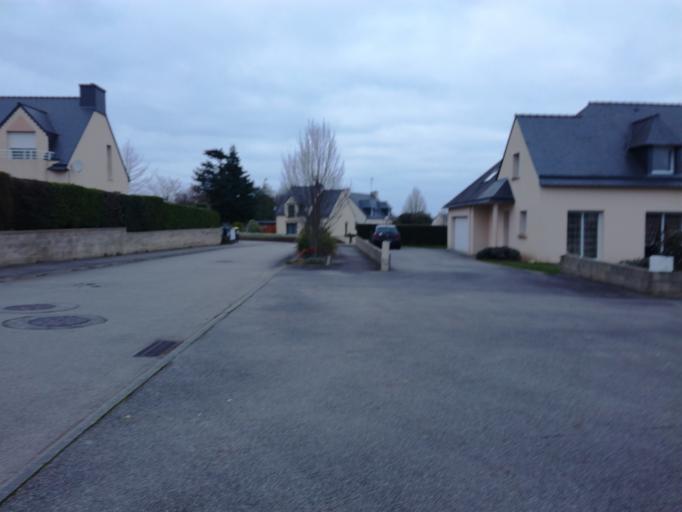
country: FR
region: Brittany
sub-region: Departement du Morbihan
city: Le Sourn
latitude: 48.0413
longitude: -2.9833
